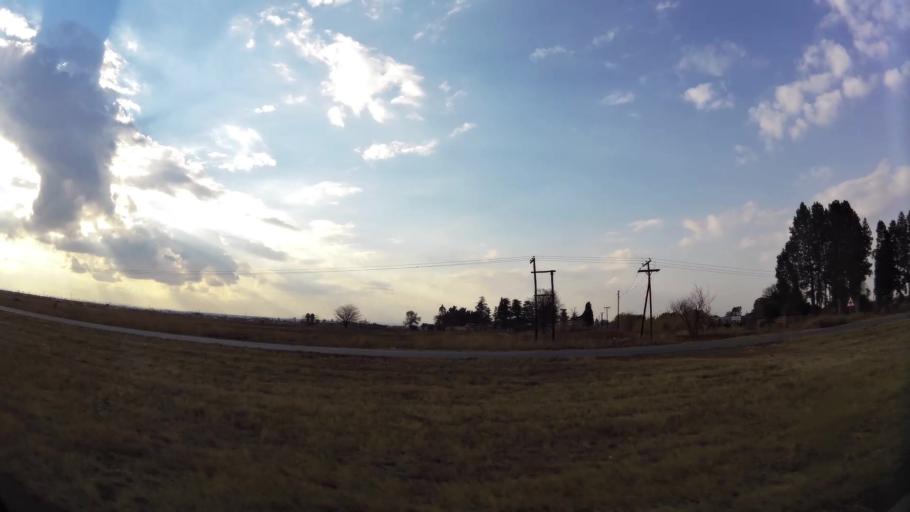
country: ZA
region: Gauteng
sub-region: Sedibeng District Municipality
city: Vanderbijlpark
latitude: -26.6196
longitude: 27.8167
